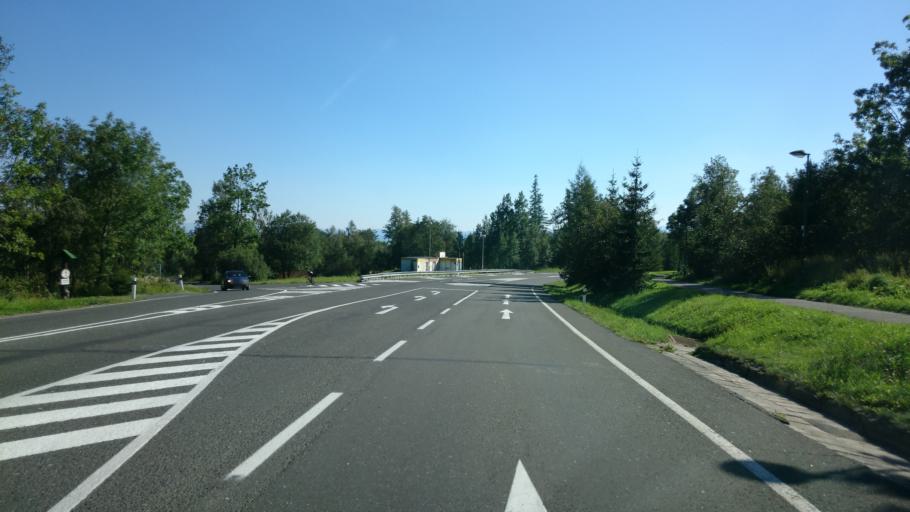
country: SK
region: Presovsky
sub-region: Okres Poprad
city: Nova Lesna
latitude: 49.1735
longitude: 20.2940
